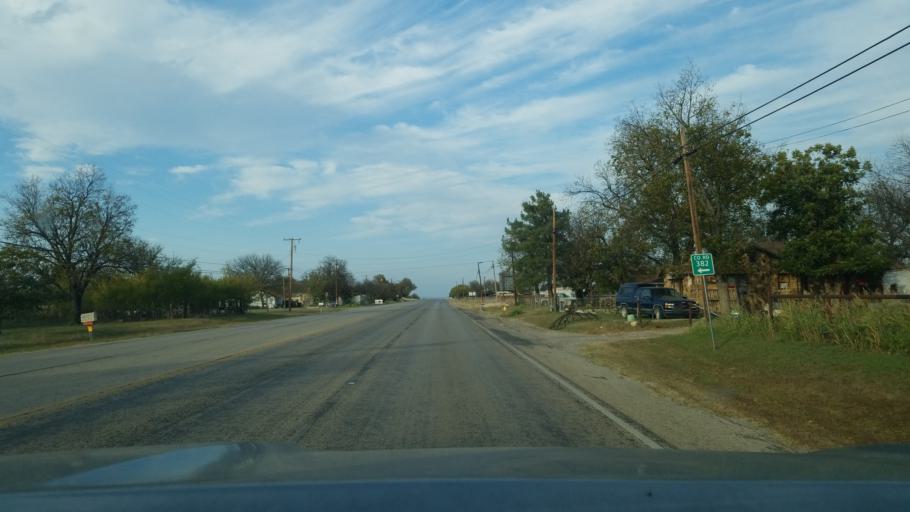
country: US
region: Texas
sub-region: Brown County
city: Early
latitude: 31.7667
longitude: -98.9547
